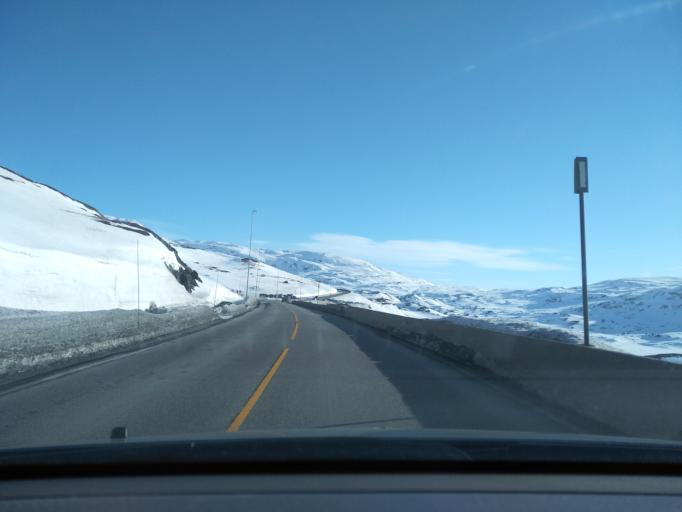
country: NO
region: Hordaland
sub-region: Odda
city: Odda
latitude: 59.8461
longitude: 6.9701
